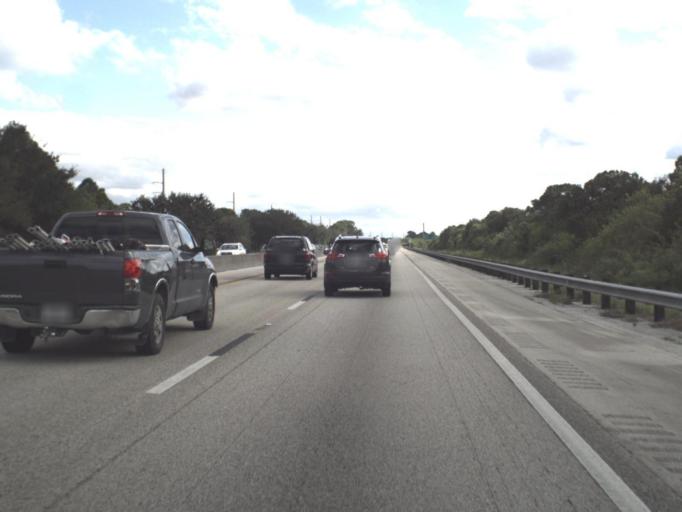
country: US
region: Florida
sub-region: Saint Lucie County
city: Port Saint Lucie
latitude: 27.2686
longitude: -80.3558
